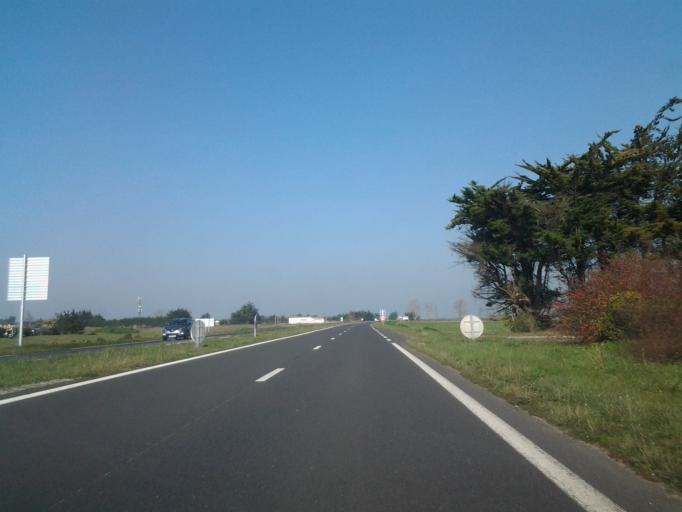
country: FR
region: Pays de la Loire
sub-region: Departement de la Vendee
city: Barbatre
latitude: 46.9381
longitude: -2.1678
